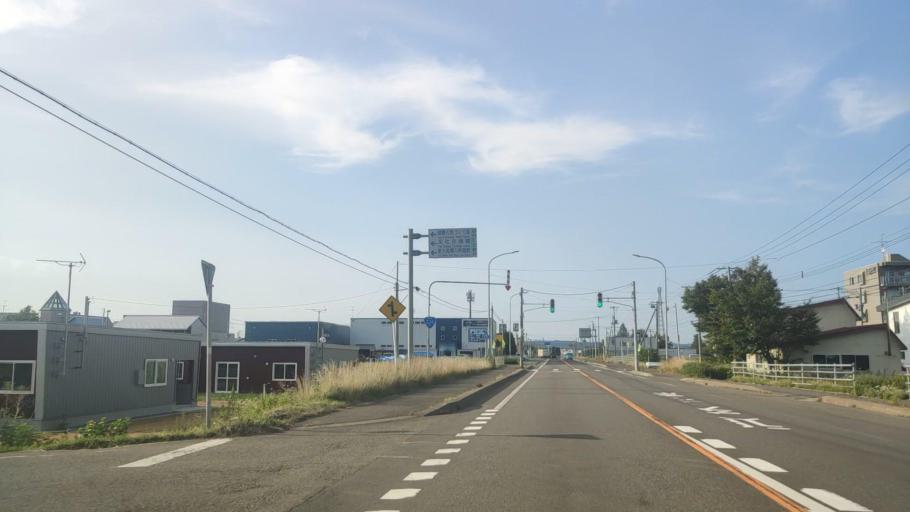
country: JP
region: Hokkaido
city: Iwamizawa
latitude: 43.0100
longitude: 141.7892
